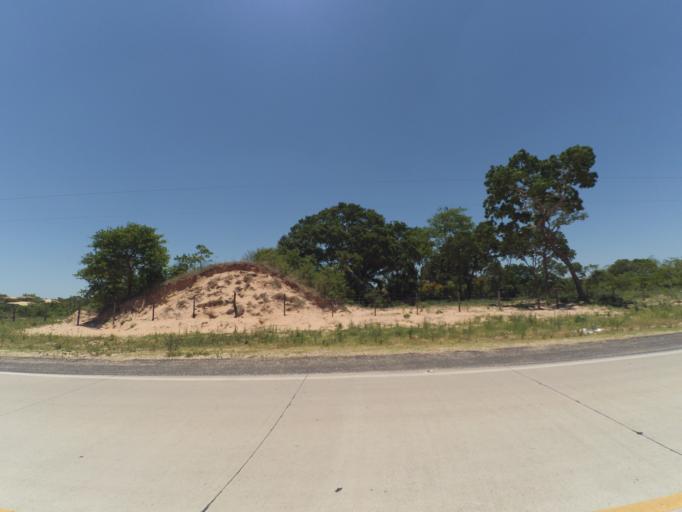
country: BO
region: Santa Cruz
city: Santa Cruz de la Sierra
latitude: -17.8160
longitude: -63.2835
